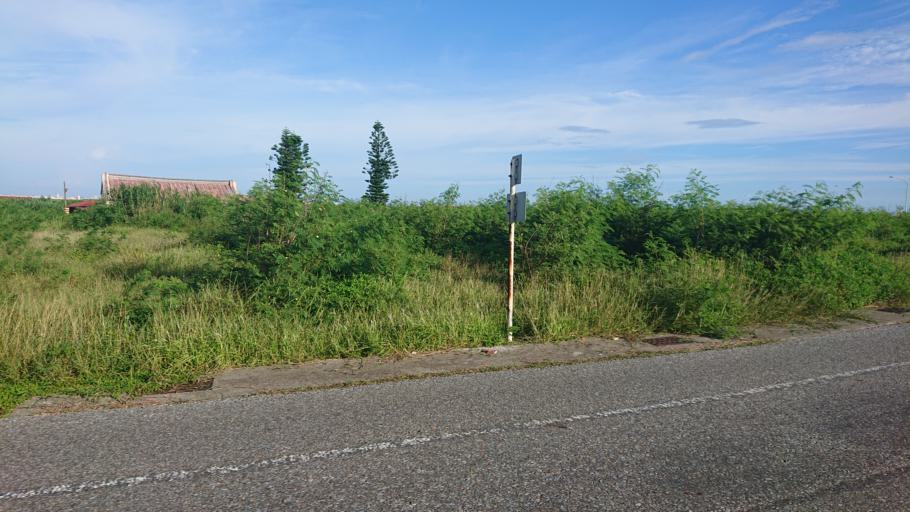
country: TW
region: Taiwan
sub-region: Penghu
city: Ma-kung
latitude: 23.6048
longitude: 119.5172
